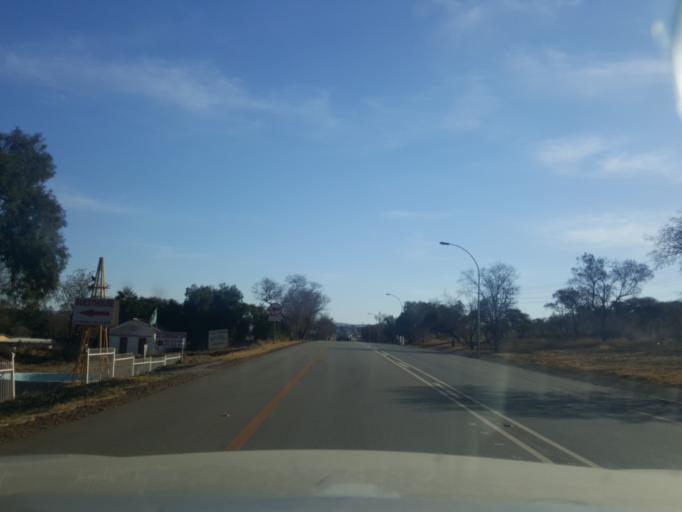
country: ZA
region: North-West
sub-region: Ngaka Modiri Molema District Municipality
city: Zeerust
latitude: -25.5420
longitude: 26.0928
